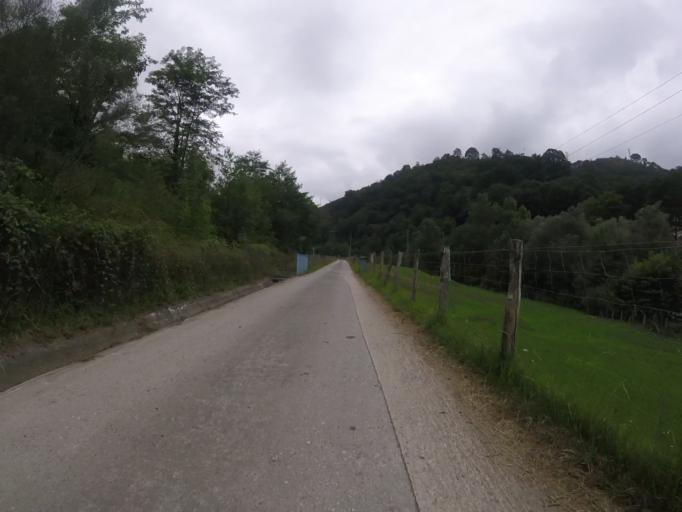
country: ES
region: Navarre
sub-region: Provincia de Navarra
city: Sunbilla
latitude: 43.1838
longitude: -1.6701
